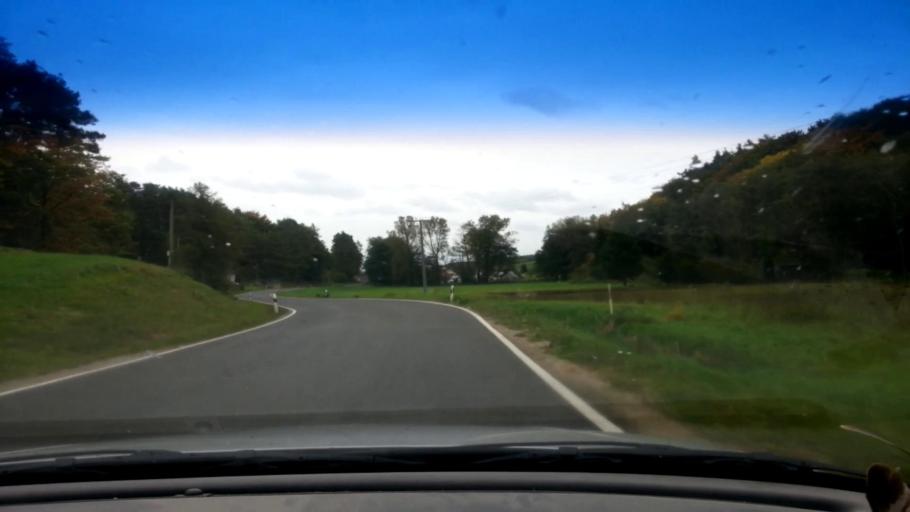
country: DE
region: Bavaria
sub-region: Upper Franconia
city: Lauter
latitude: 49.9861
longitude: 10.7635
